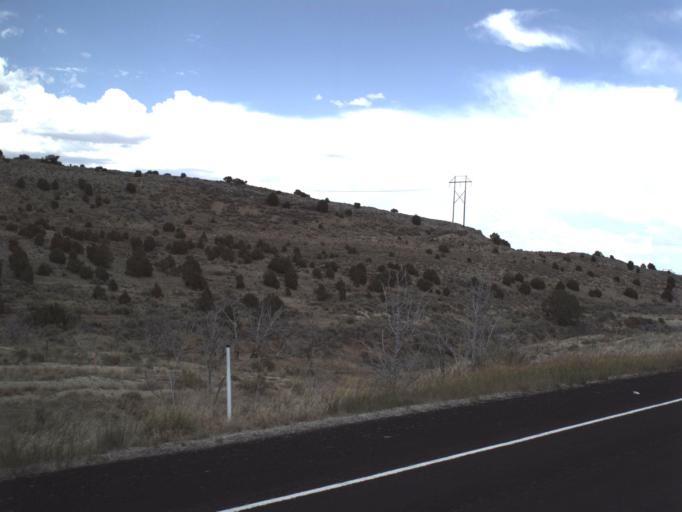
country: US
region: Idaho
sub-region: Minidoka County
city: Rupert
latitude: 41.9741
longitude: -113.1568
